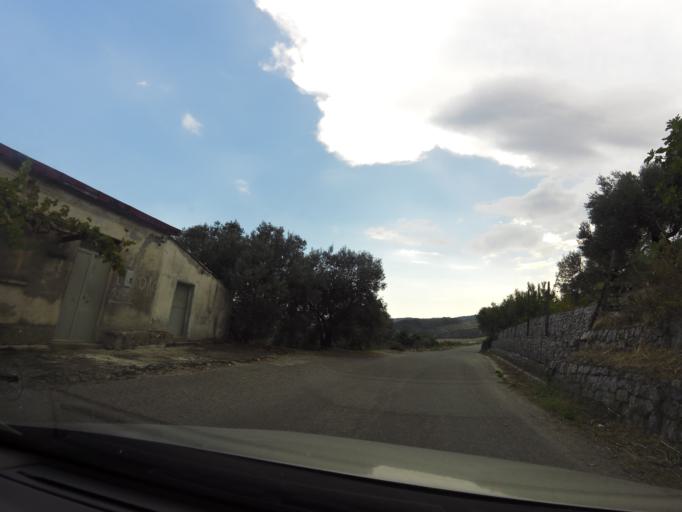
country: IT
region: Calabria
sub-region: Provincia di Reggio Calabria
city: Camini
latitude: 38.4575
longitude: 16.5041
